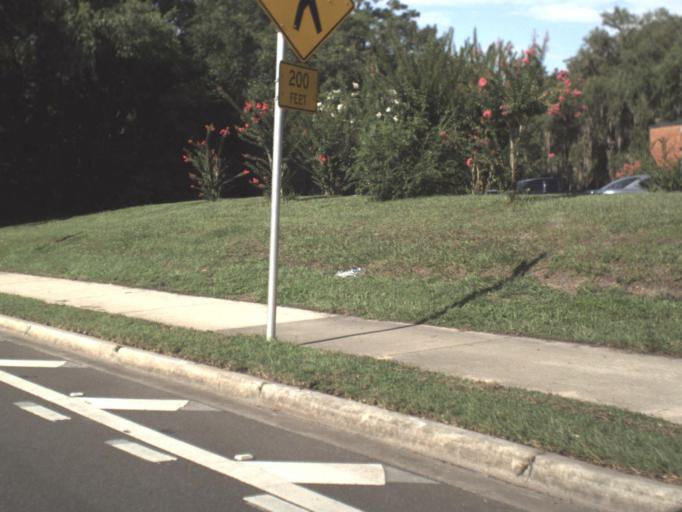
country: US
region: Florida
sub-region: Alachua County
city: Gainesville
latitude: 29.6429
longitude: -82.3394
